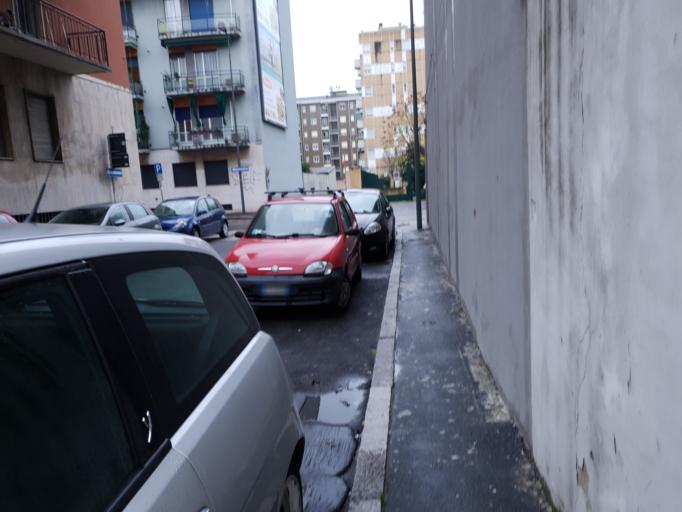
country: IT
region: Lombardy
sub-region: Citta metropolitana di Milano
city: Bresso
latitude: 45.5101
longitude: 9.1750
